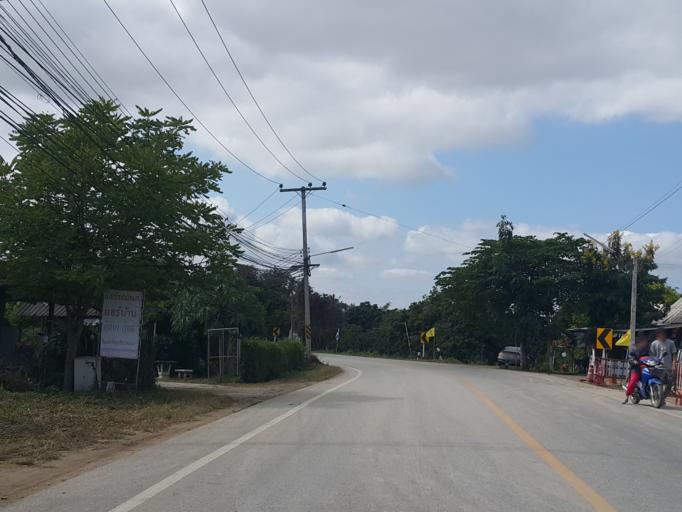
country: TH
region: Lamphun
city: Ban Thi
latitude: 18.6507
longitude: 99.1163
